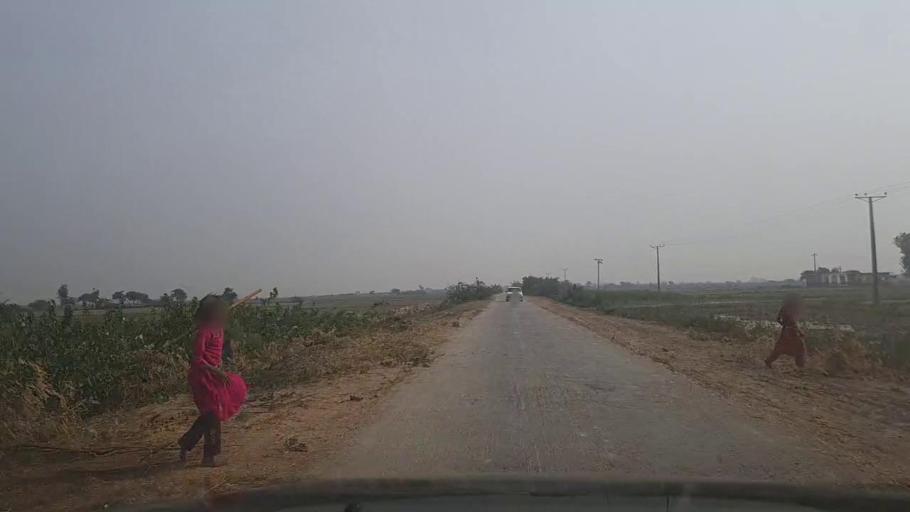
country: PK
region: Sindh
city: Mirpur Sakro
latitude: 24.4773
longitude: 67.6619
